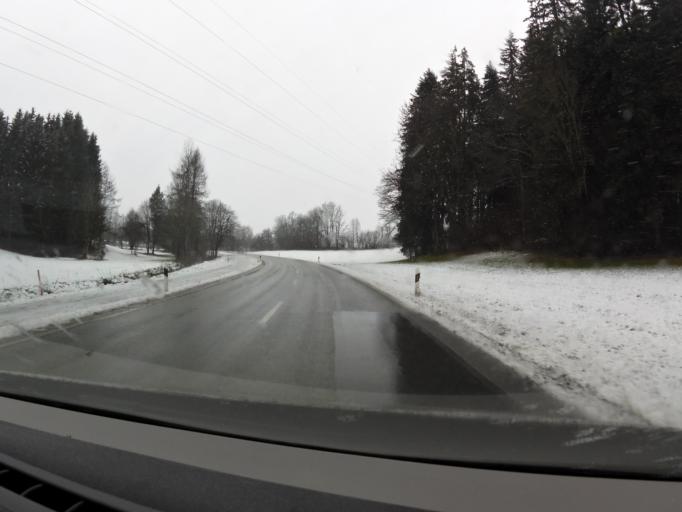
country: DE
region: Bavaria
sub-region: Upper Bavaria
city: Waakirchen
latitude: 47.7608
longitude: 11.6992
